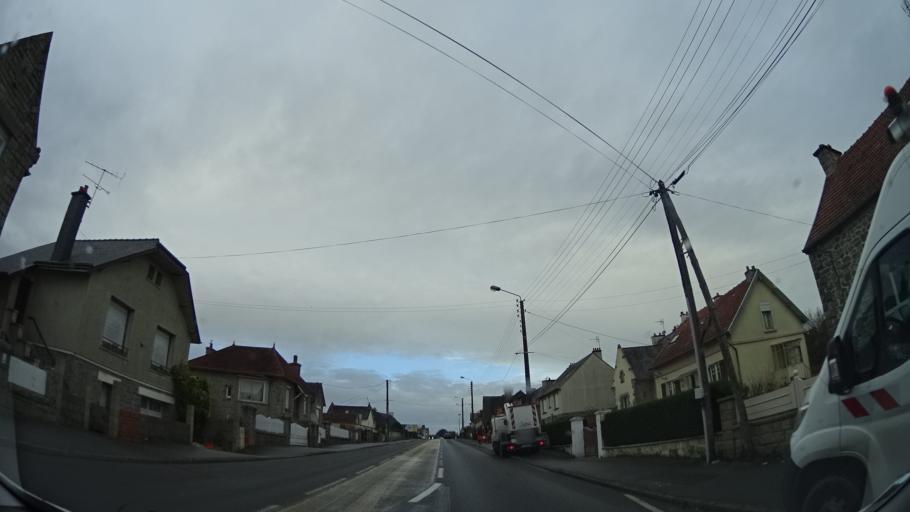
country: FR
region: Brittany
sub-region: Departement des Cotes-d'Armor
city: Quevert
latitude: 48.4476
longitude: -2.0713
